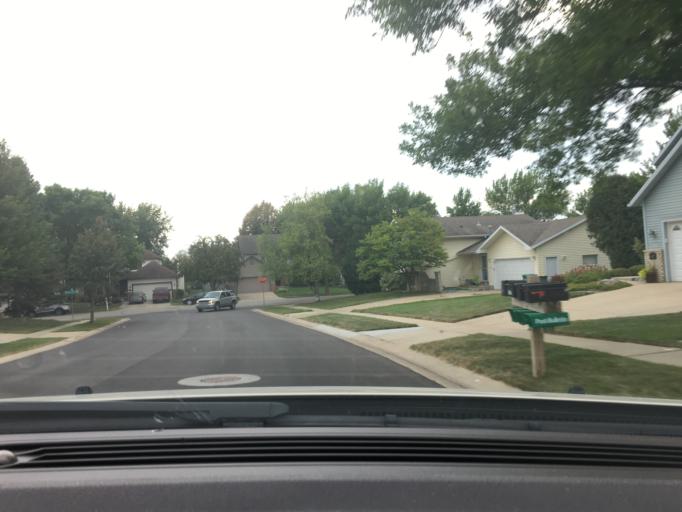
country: US
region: Minnesota
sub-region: Olmsted County
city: Oronoco
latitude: 44.0843
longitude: -92.5240
